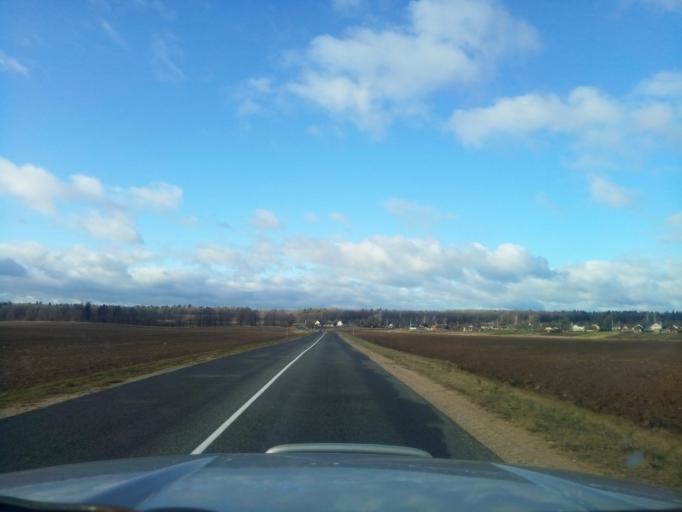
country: BY
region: Minsk
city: Kapyl'
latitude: 53.1704
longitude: 27.0409
